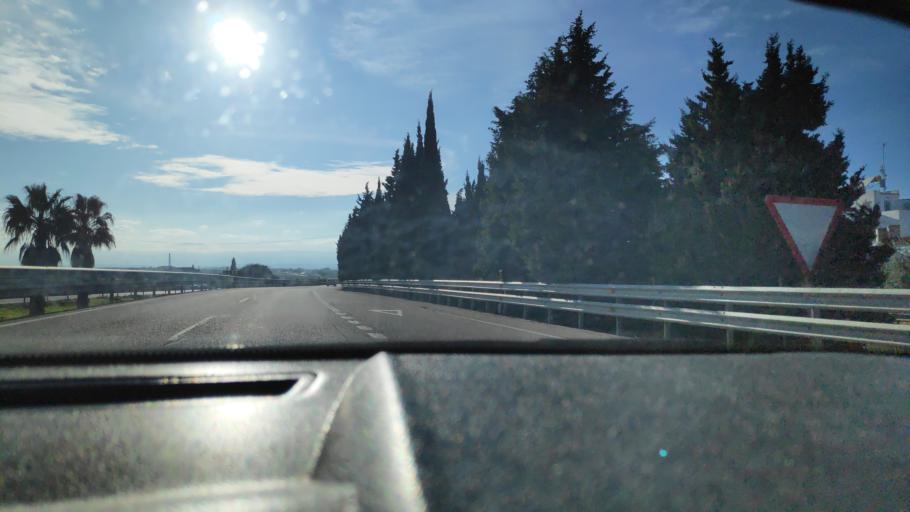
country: ES
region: Andalusia
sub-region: Province of Cordoba
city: La Carlota
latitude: 37.5899
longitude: -4.9820
